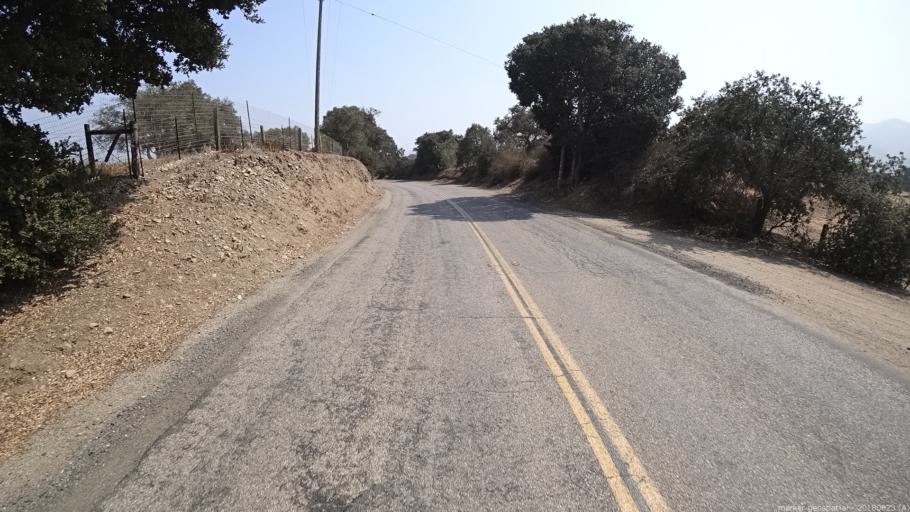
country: US
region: California
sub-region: Monterey County
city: Gonzales
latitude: 36.4640
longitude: -121.4566
